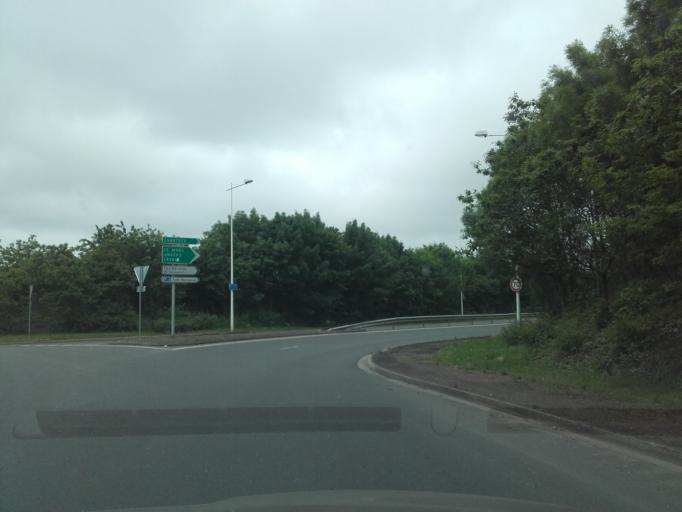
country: FR
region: Centre
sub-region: Departement d'Indre-et-Loire
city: Parcay-Meslay
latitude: 47.4202
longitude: 0.7173
